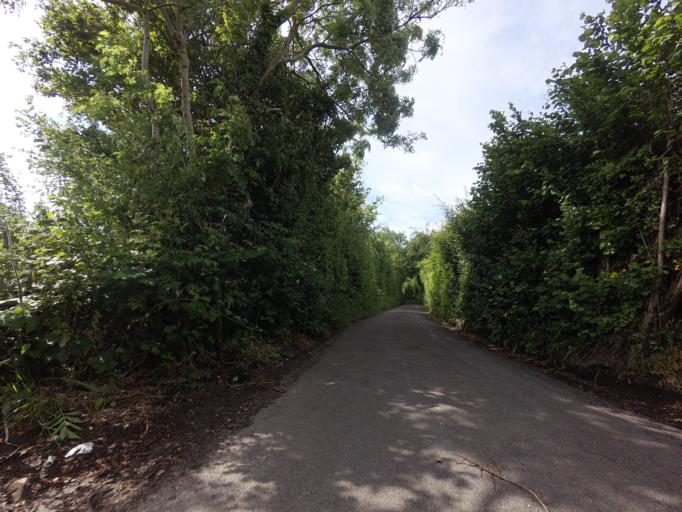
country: GB
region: England
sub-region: Greater London
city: Orpington
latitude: 51.3675
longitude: 0.1308
